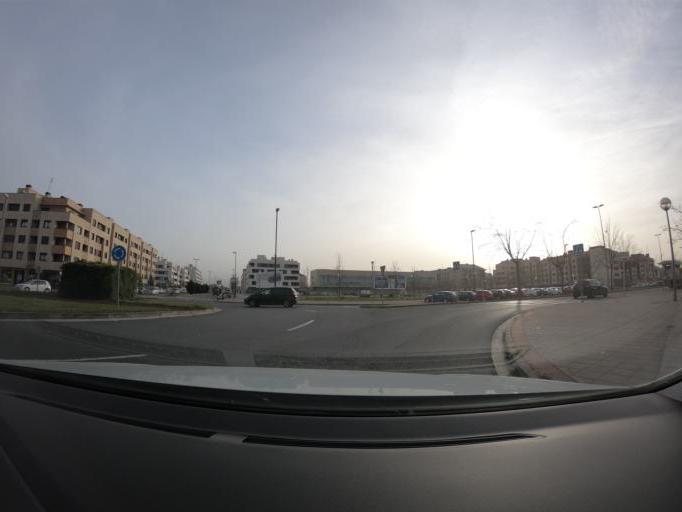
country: ES
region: La Rioja
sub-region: Provincia de La Rioja
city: Logrono
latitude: 42.4523
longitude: -2.4526
